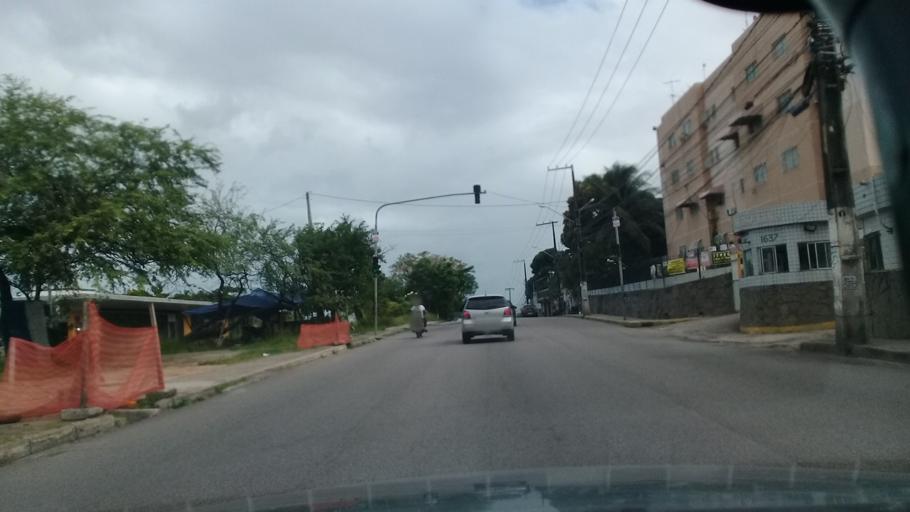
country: BR
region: Pernambuco
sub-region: Olinda
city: Olinda
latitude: -8.0053
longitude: -34.8575
